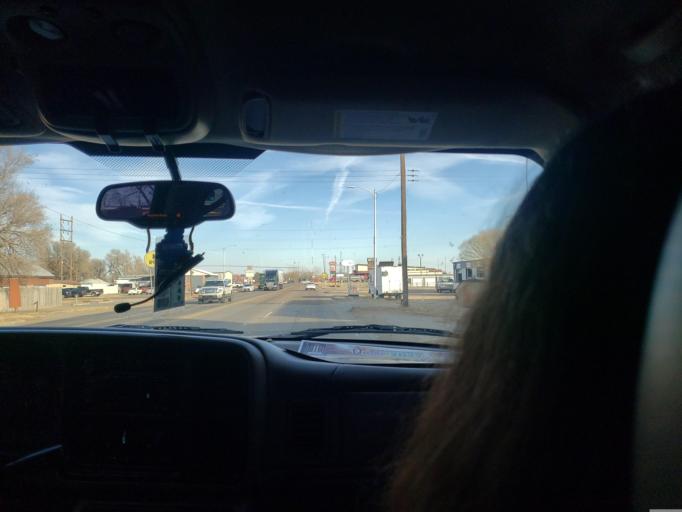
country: US
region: Oklahoma
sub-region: Texas County
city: Guymon
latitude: 36.6775
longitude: -101.4788
